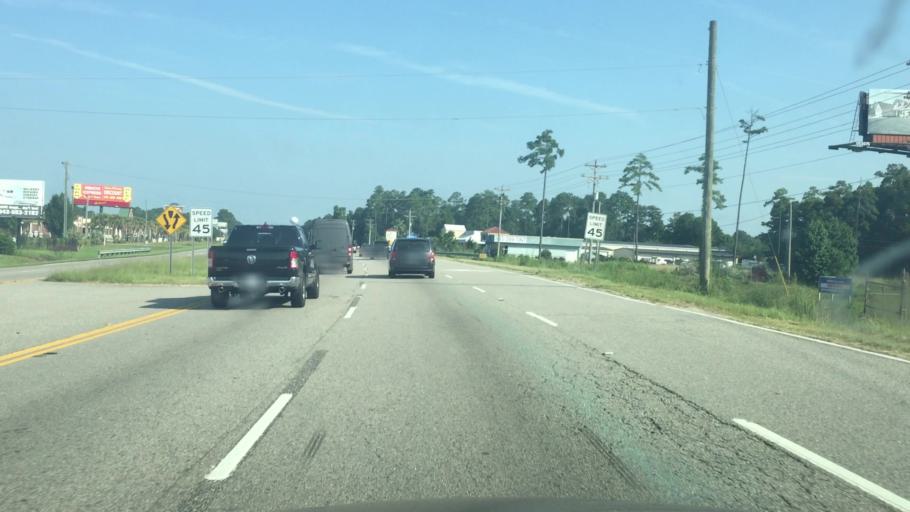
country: US
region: South Carolina
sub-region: Horry County
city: North Myrtle Beach
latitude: 33.8879
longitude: -78.6885
